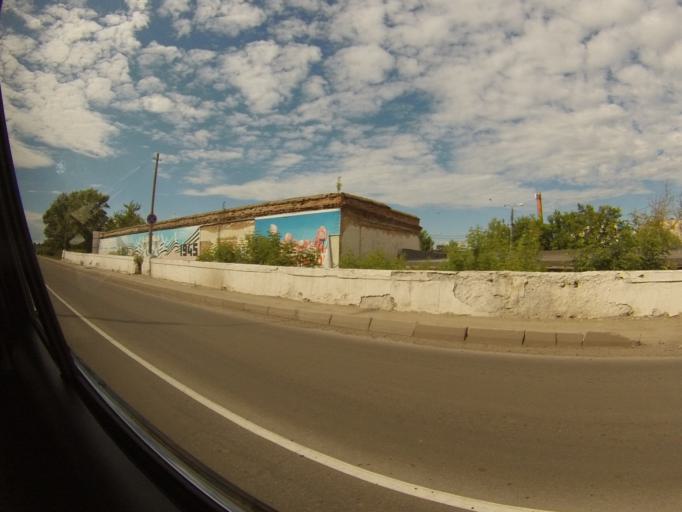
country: RU
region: Orjol
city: Mtsensk
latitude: 53.2817
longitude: 36.5688
